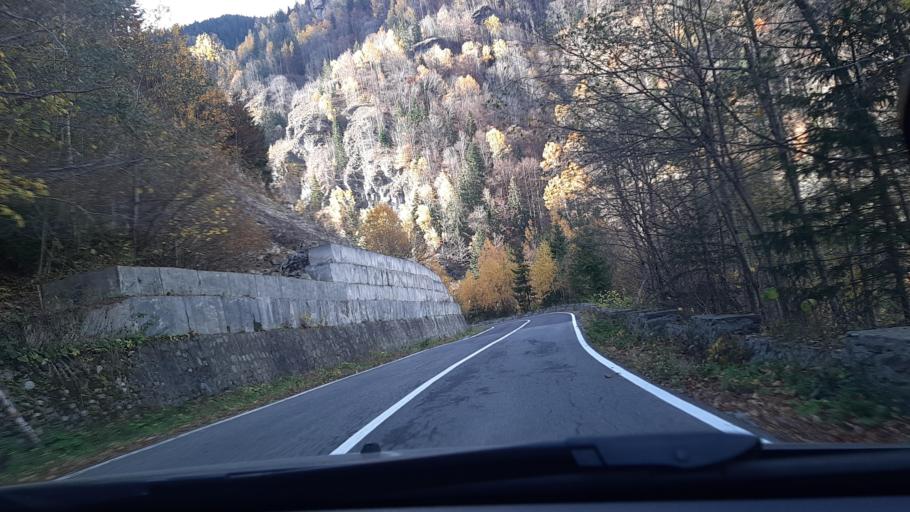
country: RO
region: Valcea
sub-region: Comuna Voineasa
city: Voineasa
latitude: 45.4360
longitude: 23.8616
